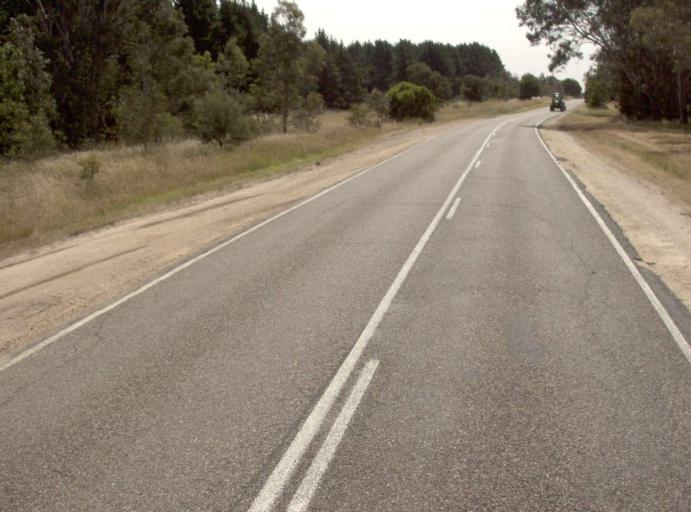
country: AU
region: Victoria
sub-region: Wellington
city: Sale
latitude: -38.1639
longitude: 146.9442
